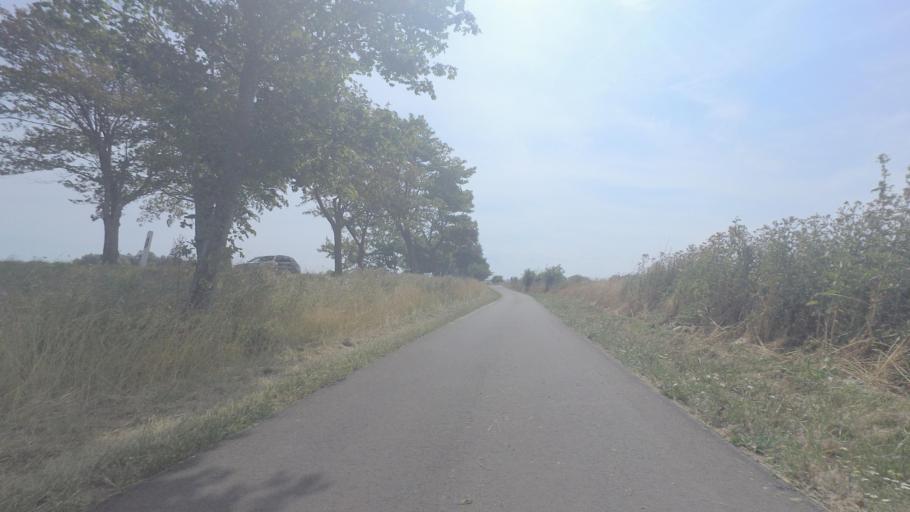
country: DE
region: Mecklenburg-Vorpommern
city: Garz
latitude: 54.2755
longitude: 13.3457
